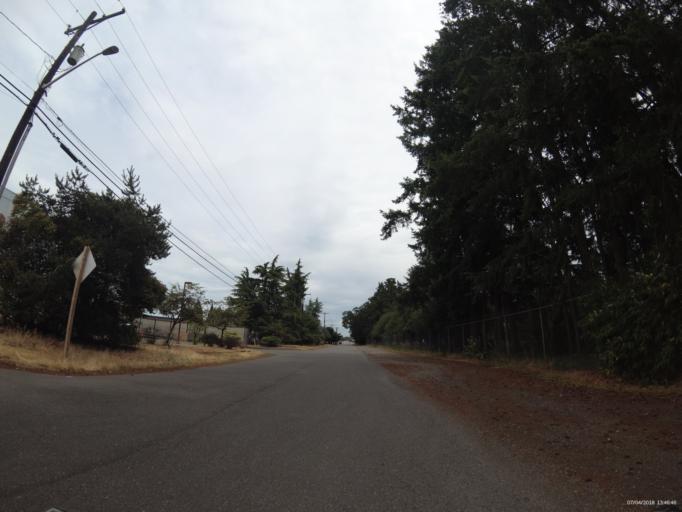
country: US
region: Washington
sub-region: Pierce County
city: McChord Air Force Base
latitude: 47.1559
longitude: -122.4872
